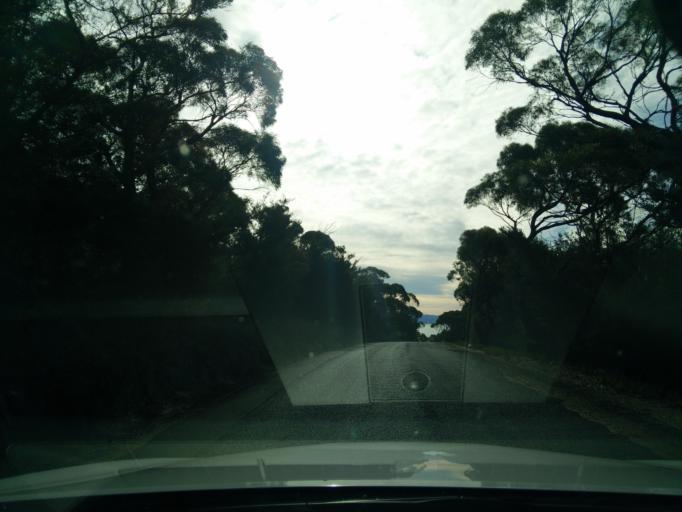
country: AU
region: Tasmania
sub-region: Break O'Day
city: St Helens
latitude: -42.1377
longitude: 148.3053
